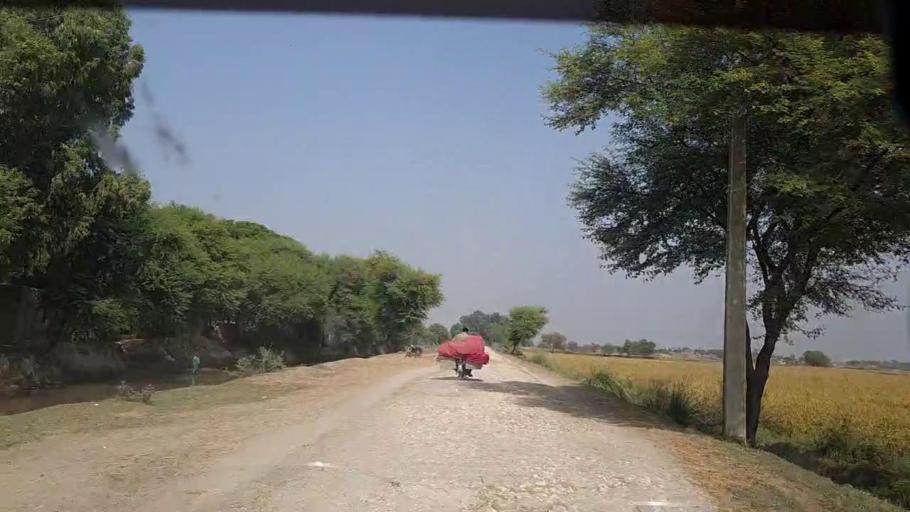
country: PK
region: Sindh
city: Thul
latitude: 28.1072
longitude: 68.6922
